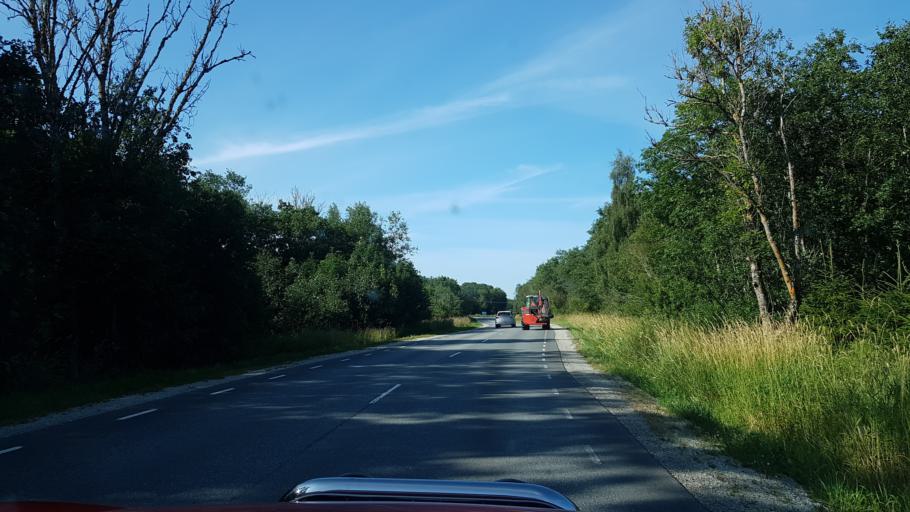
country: EE
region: Harju
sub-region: Rae vald
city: Jueri
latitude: 59.3710
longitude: 24.9227
